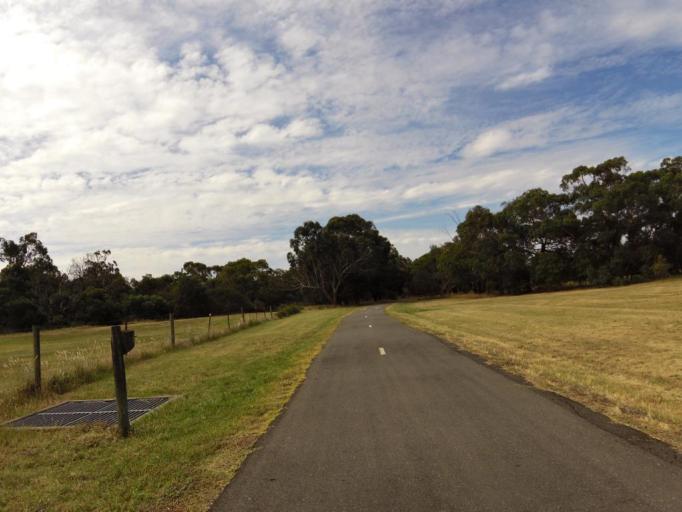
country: AU
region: Victoria
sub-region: Kingston
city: Carrum
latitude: -38.0888
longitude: 145.1370
